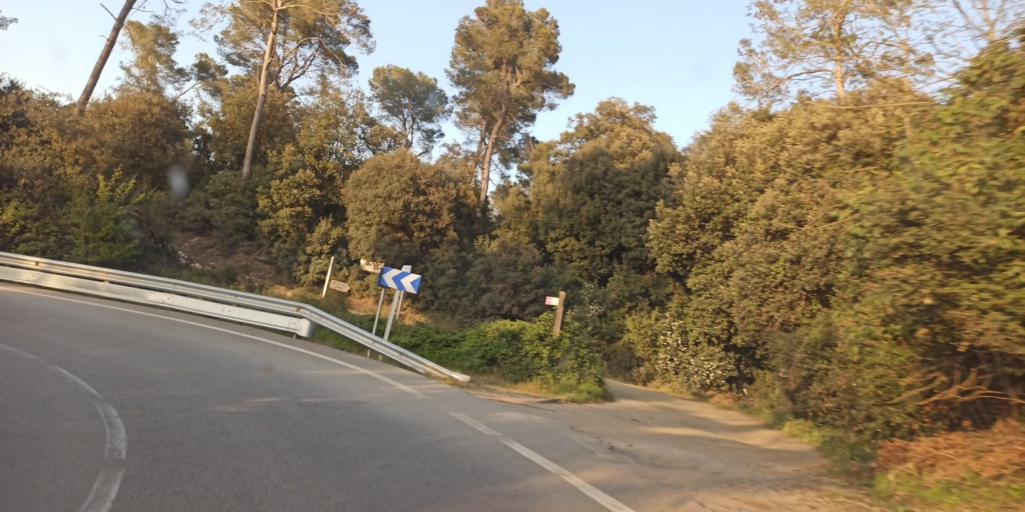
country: ES
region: Catalonia
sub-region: Provincia de Barcelona
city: Sant Cugat del Valles
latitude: 41.4524
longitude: 2.0916
